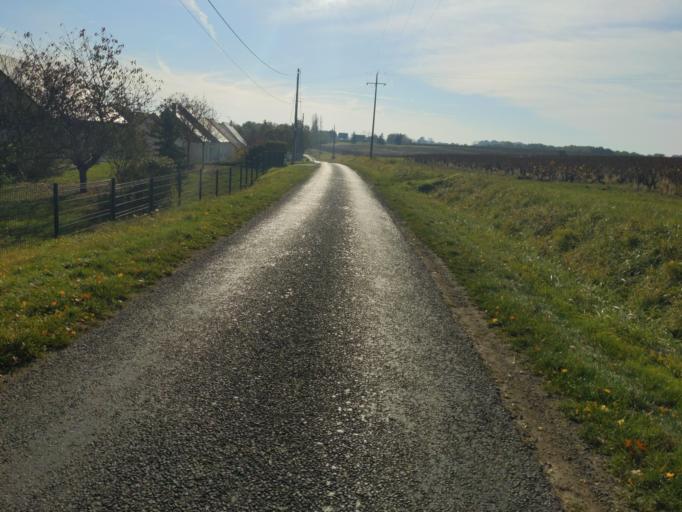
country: FR
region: Centre
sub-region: Departement d'Indre-et-Loire
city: Reugny
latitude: 47.4914
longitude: 0.8602
